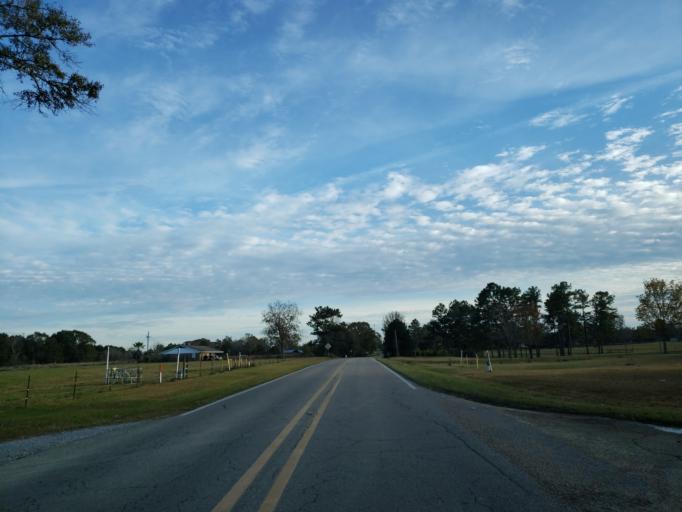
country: US
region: Mississippi
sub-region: Lamar County
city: Purvis
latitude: 31.1713
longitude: -89.4268
